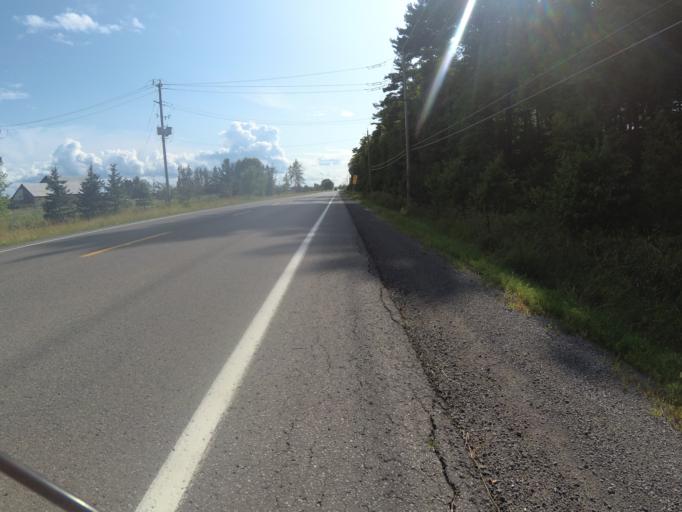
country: CA
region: Ontario
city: Arnprior
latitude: 45.4184
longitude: -76.2653
